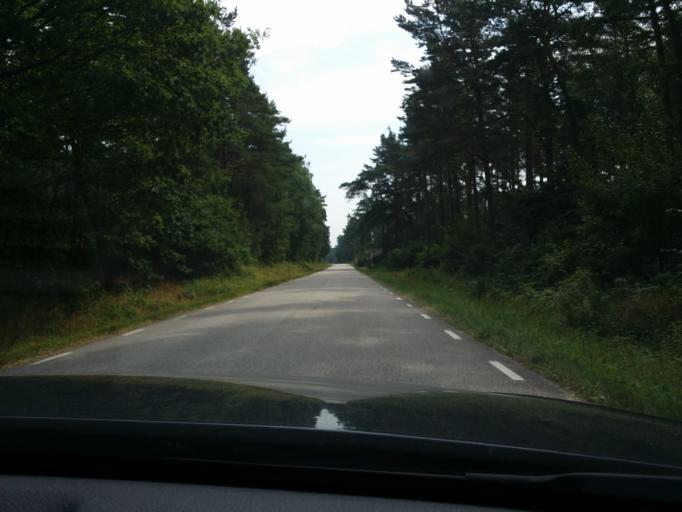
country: SE
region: Blekinge
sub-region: Solvesborgs Kommun
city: Soelvesborg
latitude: 56.0287
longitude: 14.6976
